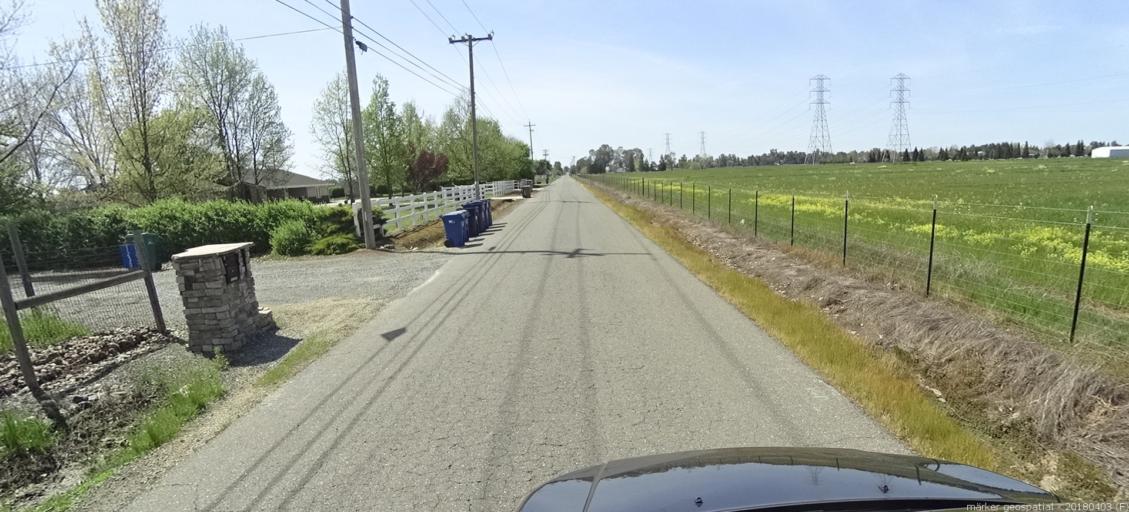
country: US
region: California
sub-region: Sacramento County
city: Clay
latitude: 38.3505
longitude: -121.2111
